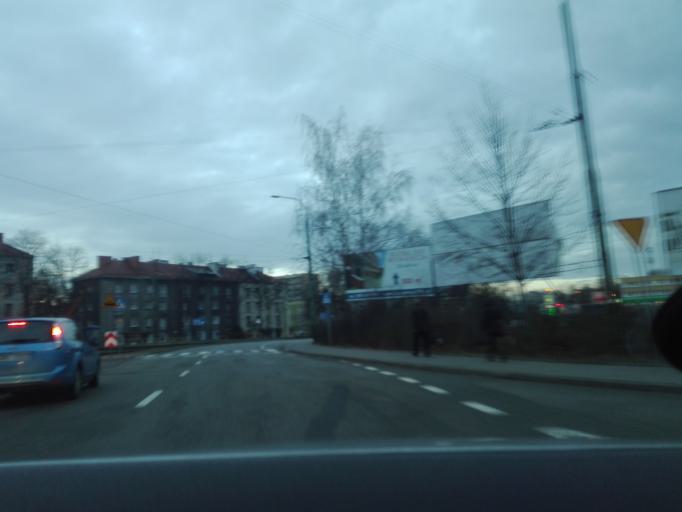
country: PL
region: Silesian Voivodeship
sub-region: Katowice
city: Katowice
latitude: 50.2741
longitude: 19.0251
